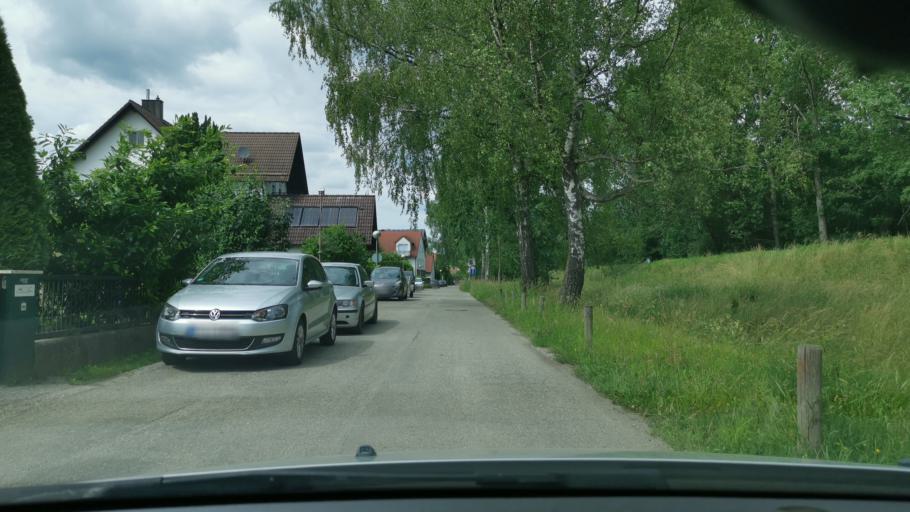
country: DE
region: Bavaria
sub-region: Upper Bavaria
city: Moosburg
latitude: 48.4678
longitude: 11.9467
